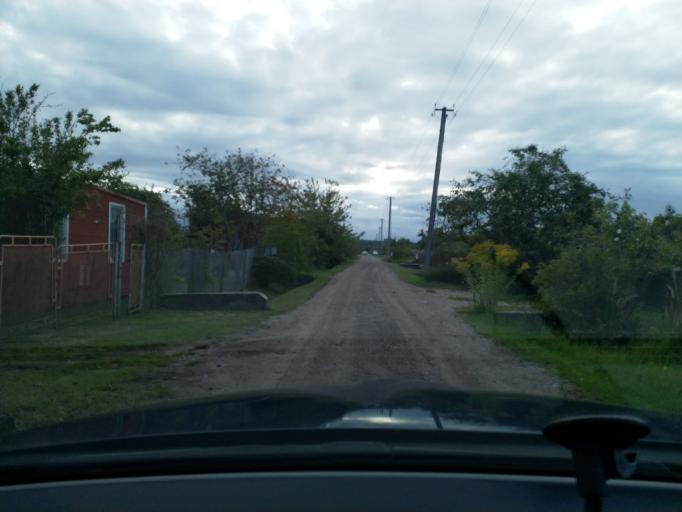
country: LV
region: Kuldigas Rajons
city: Kuldiga
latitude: 56.9533
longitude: 21.9791
